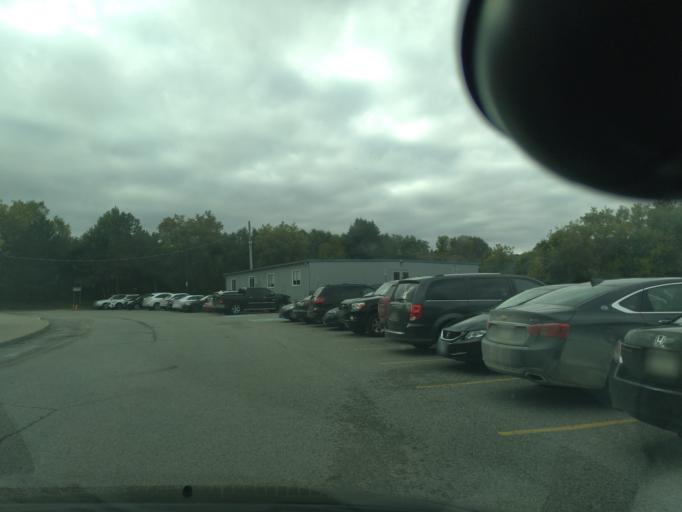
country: CA
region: Ontario
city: Newmarket
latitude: 44.0568
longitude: -79.4405
